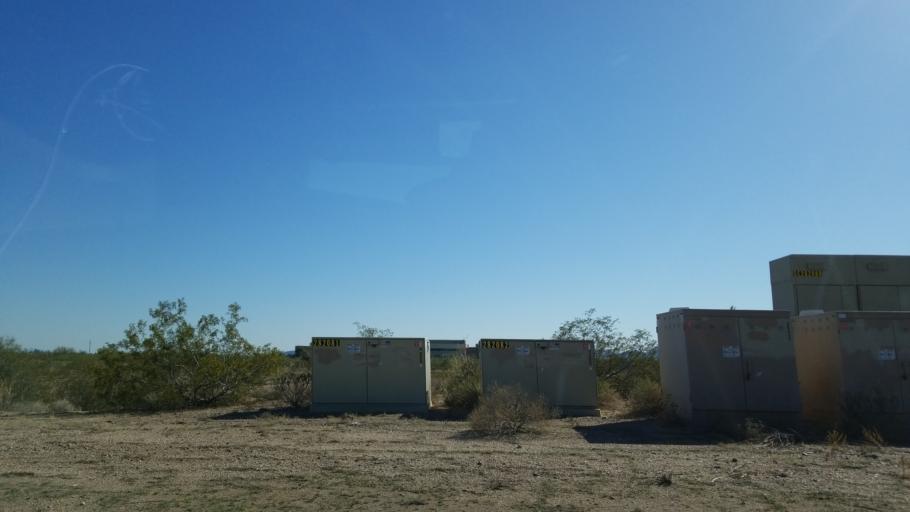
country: US
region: Arizona
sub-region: Maricopa County
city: Paradise Valley
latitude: 33.6636
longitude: -111.9627
